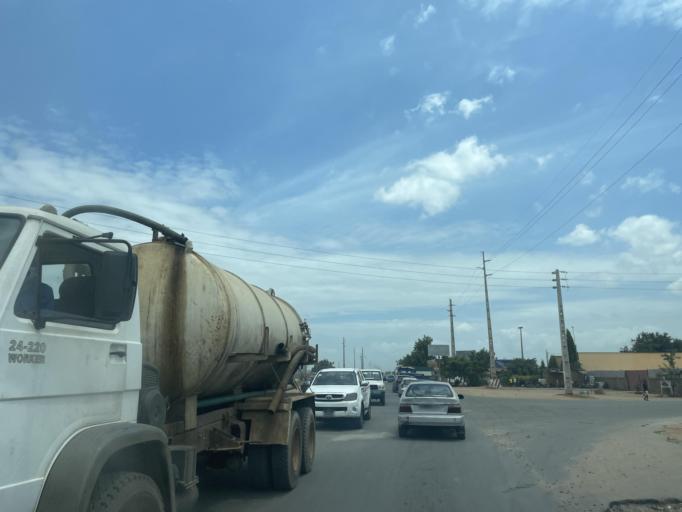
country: AO
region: Luanda
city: Luanda
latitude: -8.9448
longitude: 13.3845
